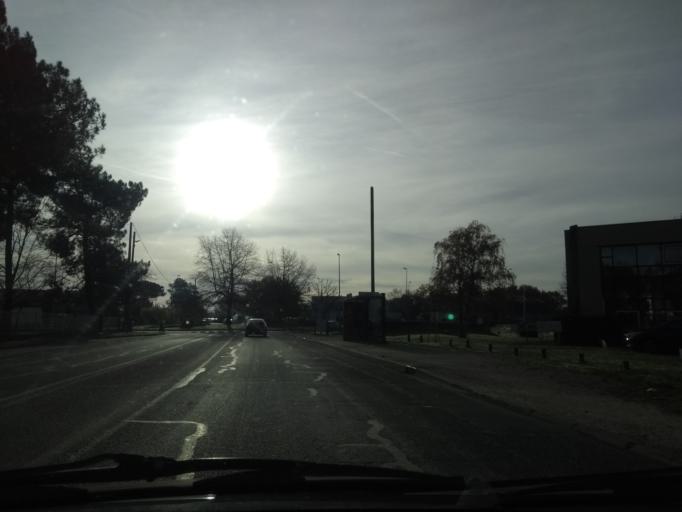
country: FR
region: Aquitaine
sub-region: Departement de la Gironde
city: Canejan
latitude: 44.7841
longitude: -0.6531
